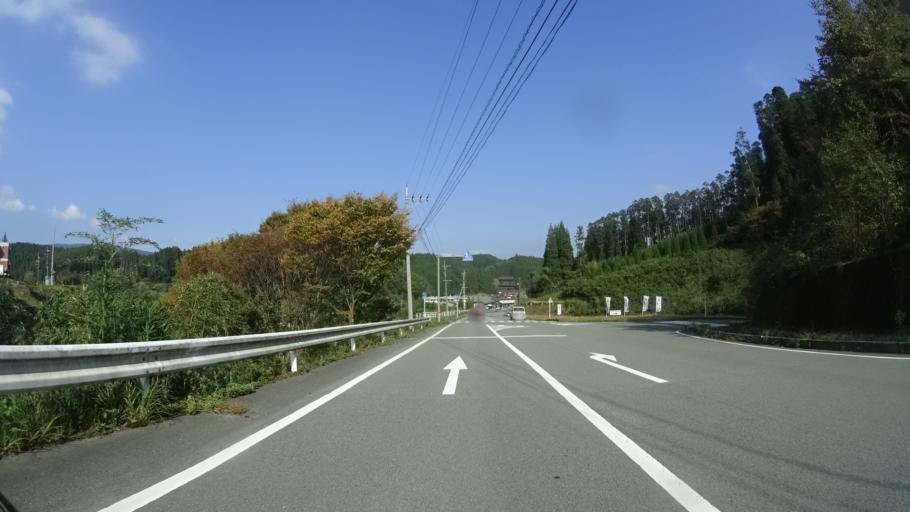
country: JP
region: Oita
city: Tsukawaki
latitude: 33.1397
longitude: 131.0916
